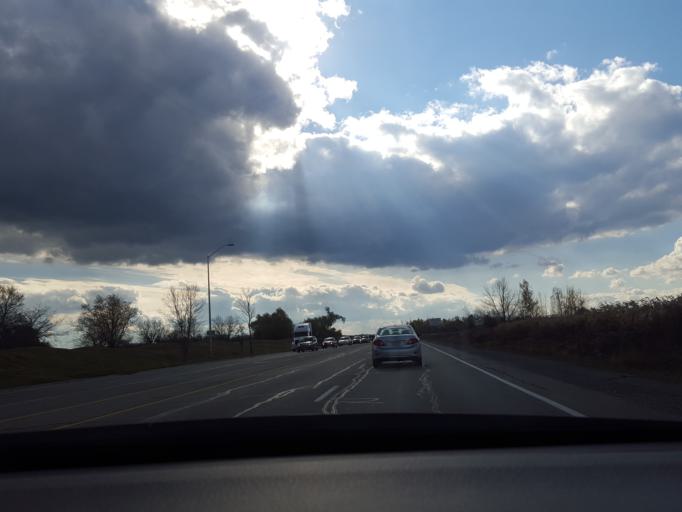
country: CA
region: Ontario
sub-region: Halton
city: Milton
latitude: 43.5443
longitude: -79.8205
